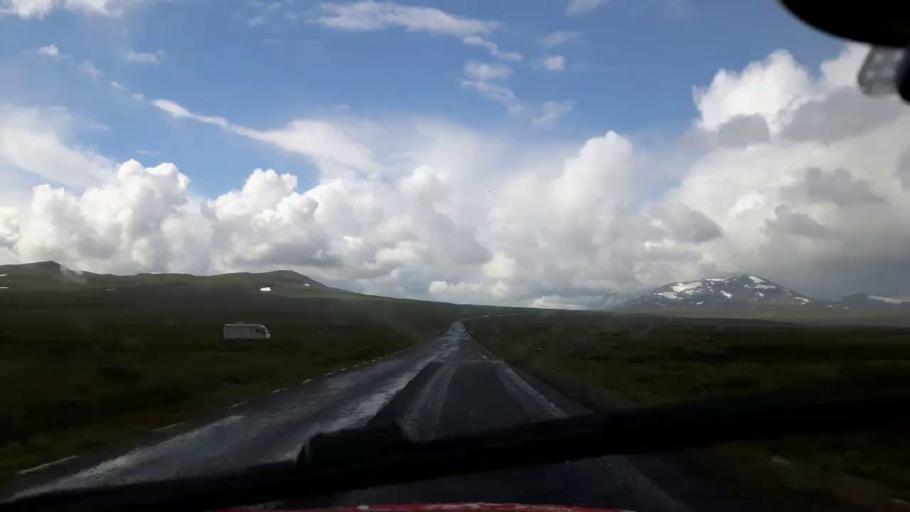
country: NO
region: Nordland
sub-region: Hattfjelldal
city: Hattfjelldal
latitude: 65.0844
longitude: 14.4533
